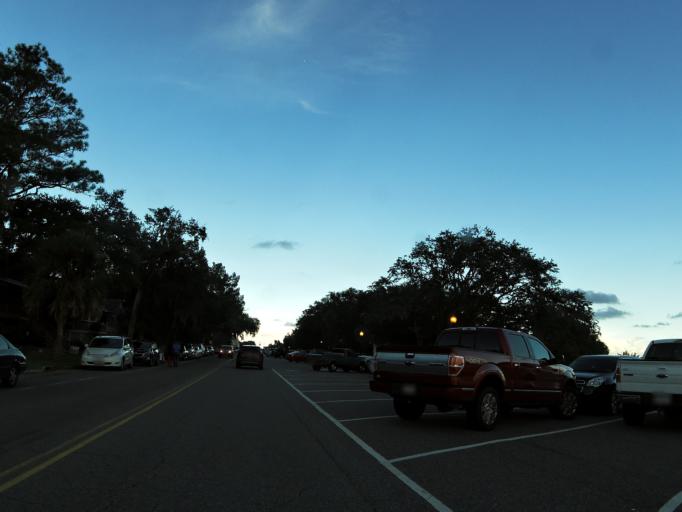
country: US
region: Georgia
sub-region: Camden County
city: St. Marys
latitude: 30.7211
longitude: -81.5527
